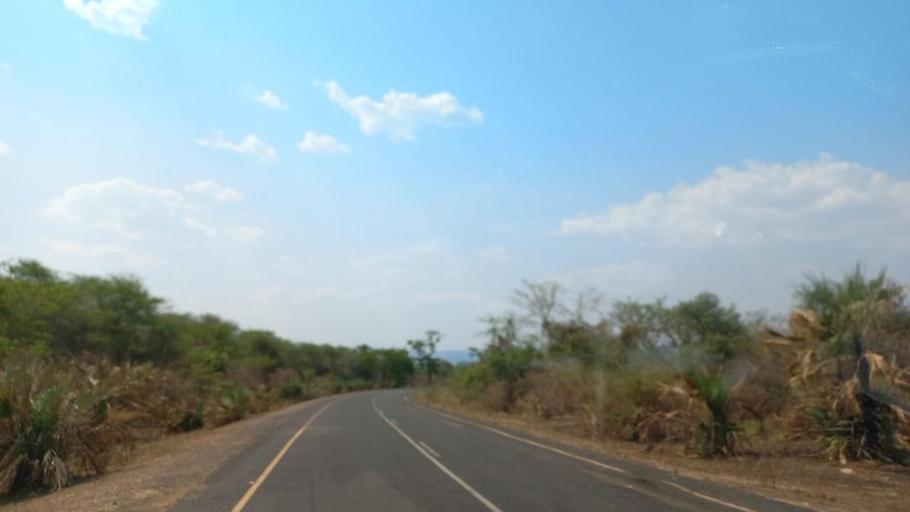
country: ZM
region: Lusaka
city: Luangwa
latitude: -15.1021
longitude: 30.1947
